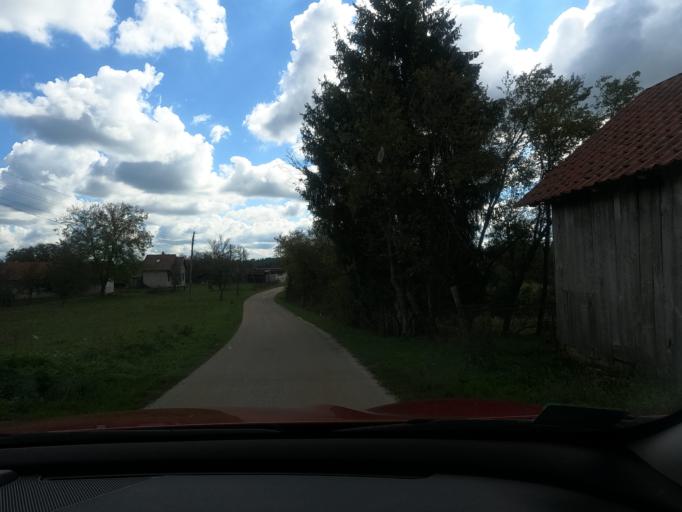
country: HR
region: Karlovacka
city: Vojnic
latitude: 45.2449
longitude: 15.7109
